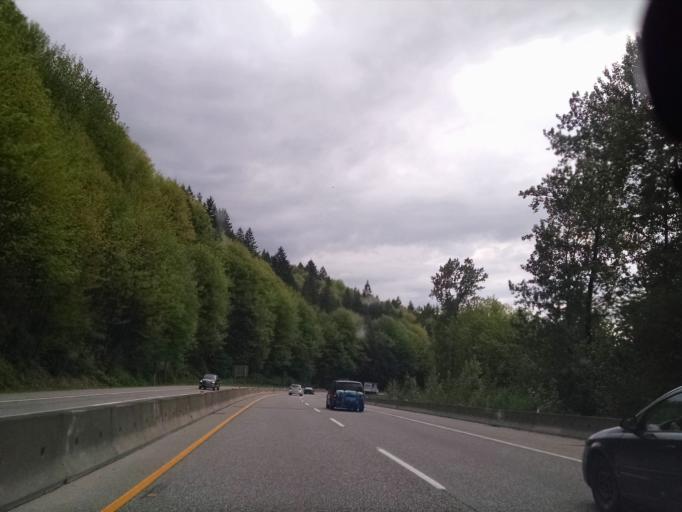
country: CA
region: British Columbia
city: Agassiz
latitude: 49.1741
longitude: -121.7757
